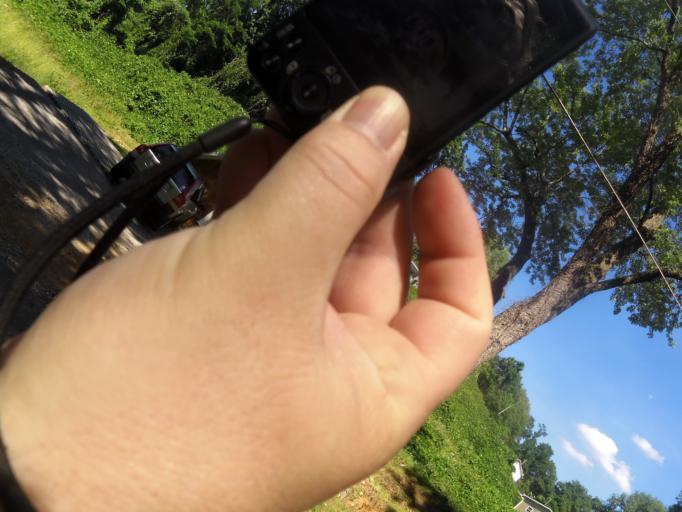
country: US
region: Tennessee
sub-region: Knox County
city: Knoxville
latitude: 35.9528
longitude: -83.9086
